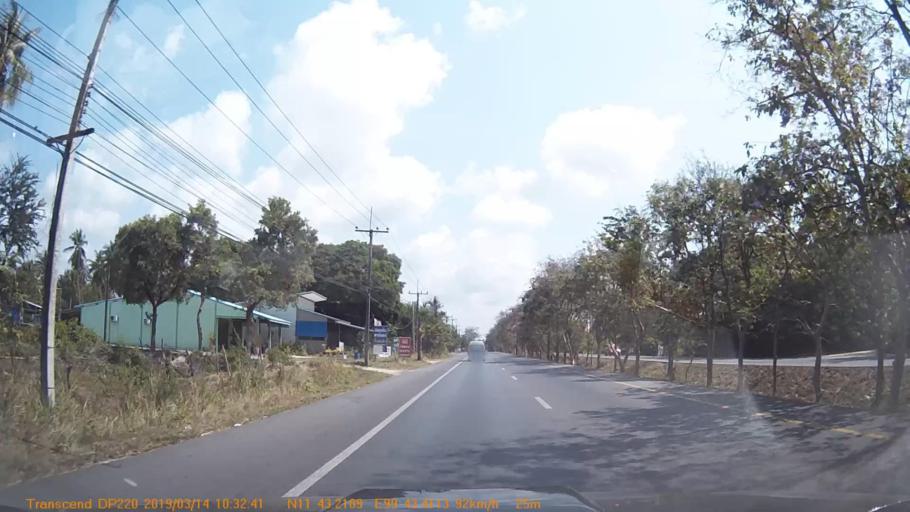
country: TH
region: Prachuap Khiri Khan
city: Prachuap Khiri Khan
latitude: 11.7107
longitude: 99.7167
